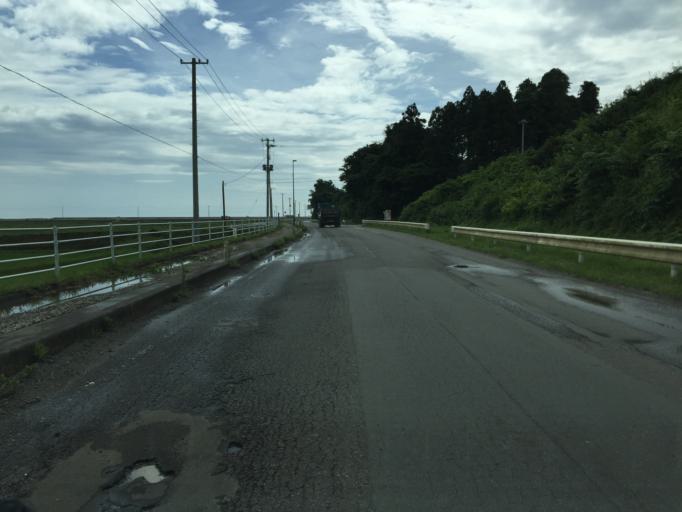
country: JP
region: Miyagi
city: Marumori
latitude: 37.7679
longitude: 140.9761
